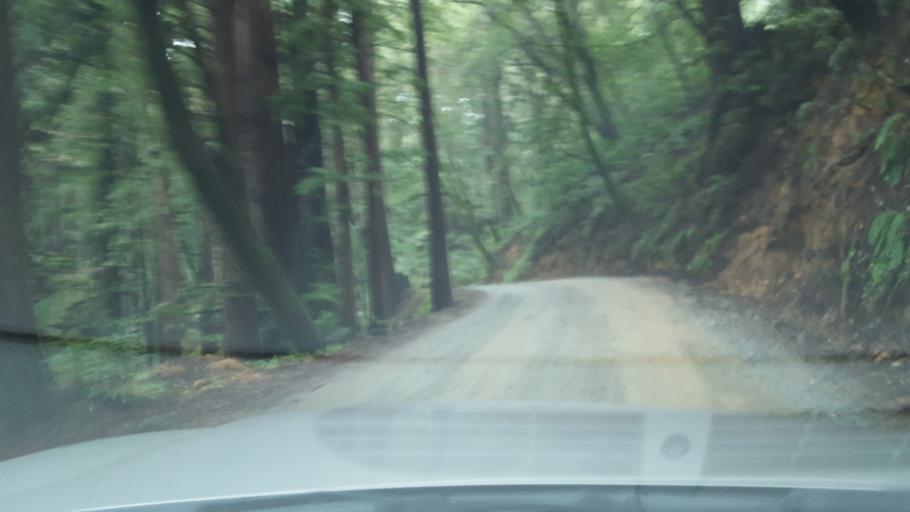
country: US
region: California
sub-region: Santa Cruz County
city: Interlaken
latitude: 37.0170
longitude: -121.7168
